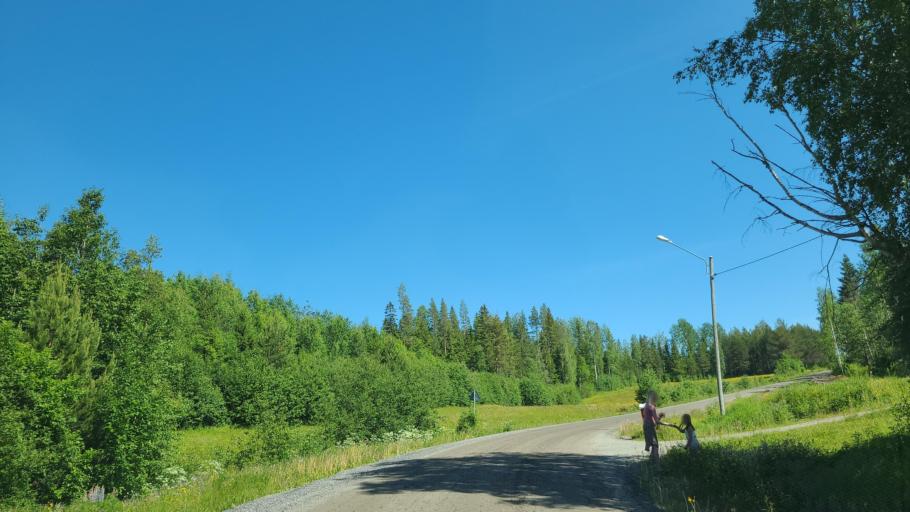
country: SE
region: Vaesterbotten
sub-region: Bjurholms Kommun
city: Bjurholm
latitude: 63.6423
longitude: 19.0986
